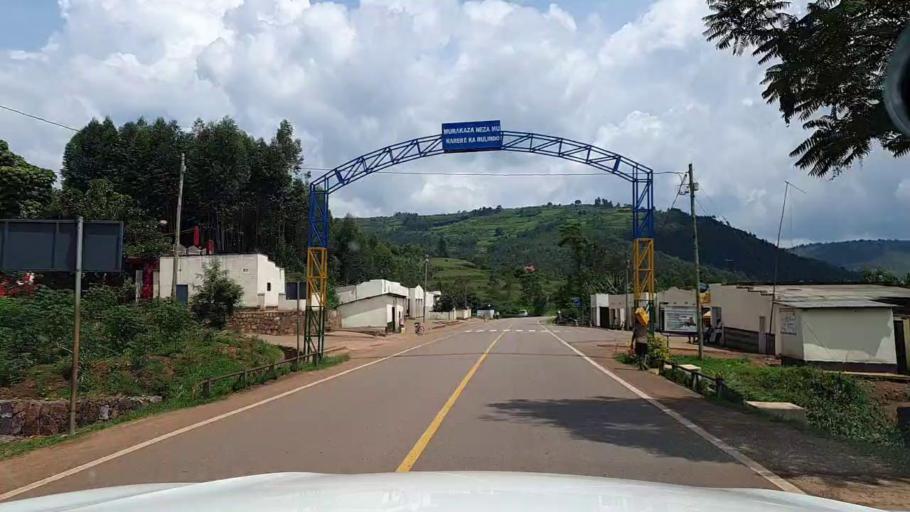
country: RW
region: Kigali
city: Kigali
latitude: -1.8262
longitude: 30.0795
